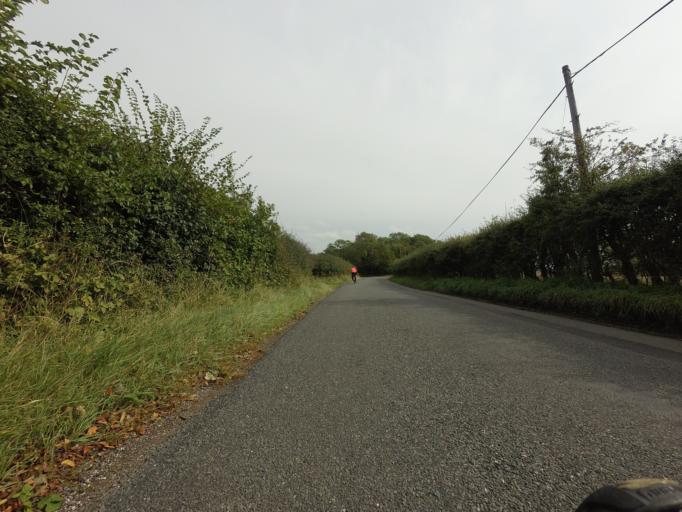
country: GB
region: England
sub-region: Cambridgeshire
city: Duxford
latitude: 52.0222
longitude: 0.1602
